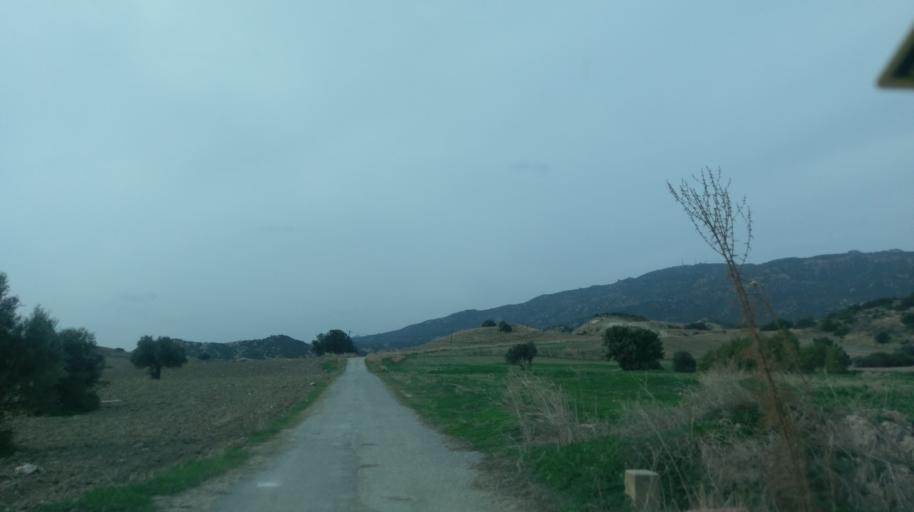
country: CY
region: Ammochostos
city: Trikomo
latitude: 35.3630
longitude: 33.9170
